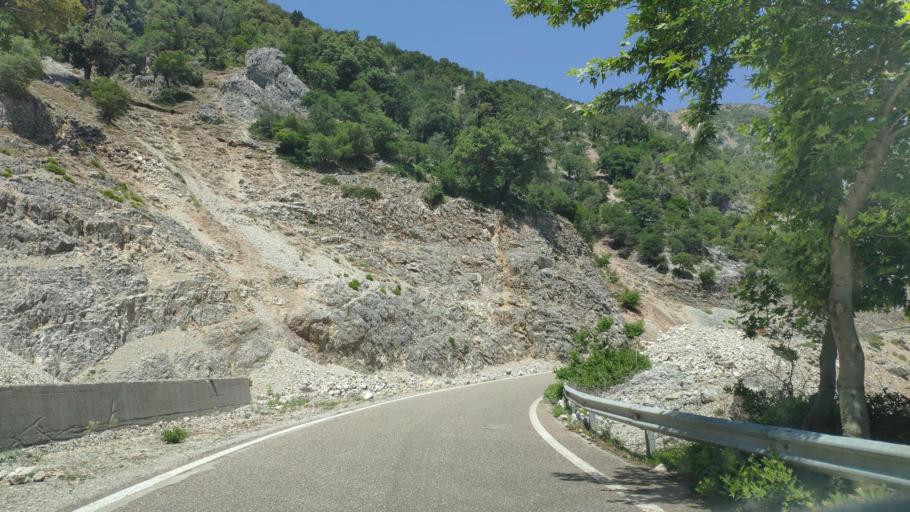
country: GR
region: West Greece
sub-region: Nomos Aitolias kai Akarnanias
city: Krikellos
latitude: 39.0159
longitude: 21.3700
